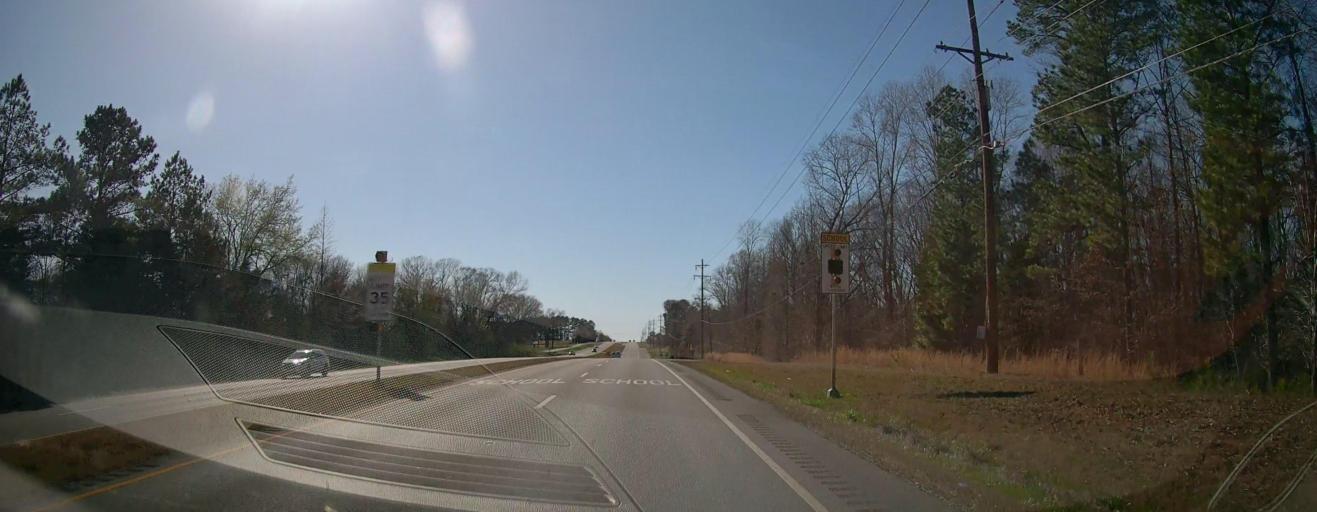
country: US
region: Alabama
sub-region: Lauderdale County
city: Killen
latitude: 34.8598
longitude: -87.4893
